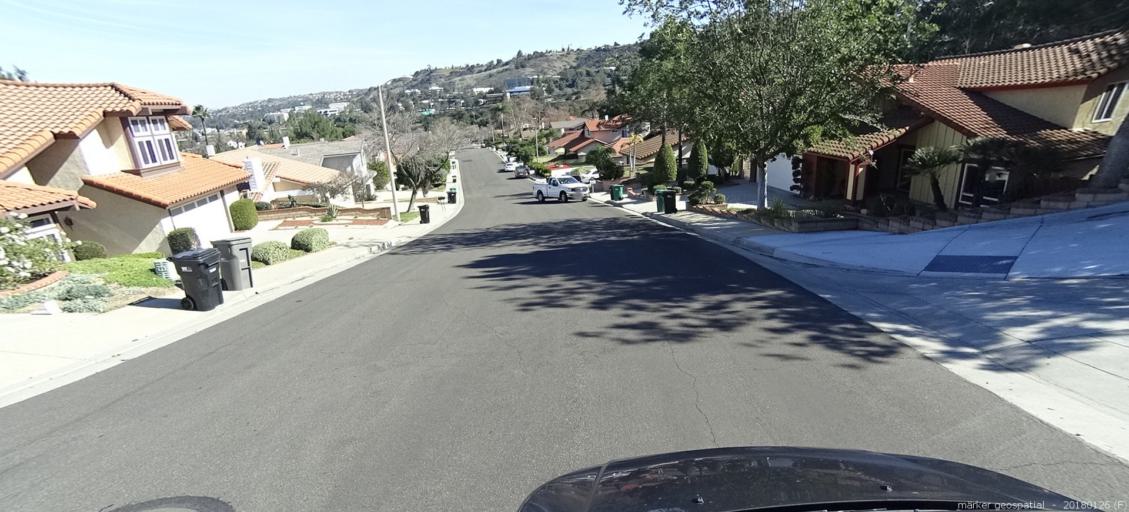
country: US
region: California
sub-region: Los Angeles County
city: Walnut
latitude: 33.9957
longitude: -117.8465
